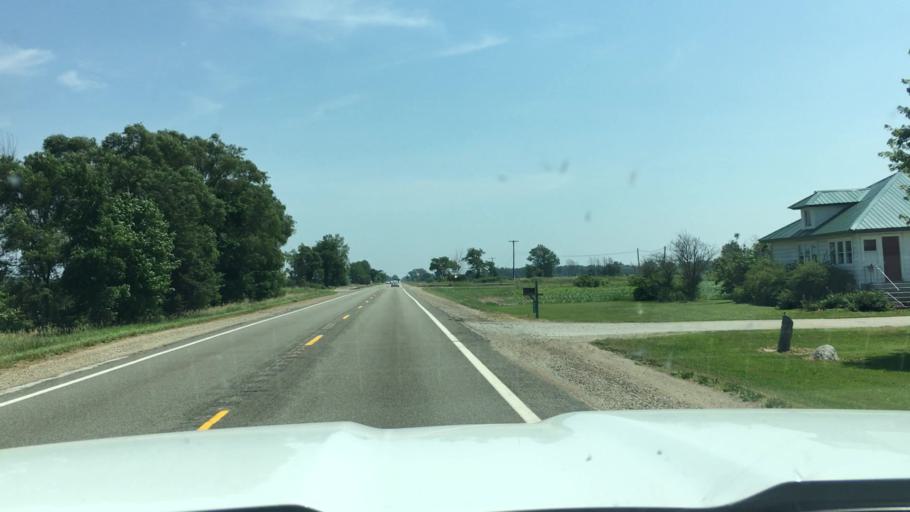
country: US
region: Michigan
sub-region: Gratiot County
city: Ithaca
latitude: 43.1758
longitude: -84.4698
